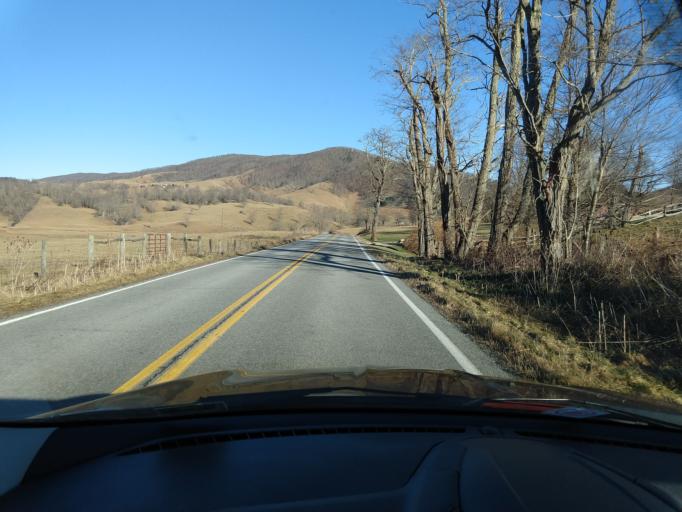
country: US
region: Virginia
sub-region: Highland County
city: Monterey
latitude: 38.3773
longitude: -79.6571
